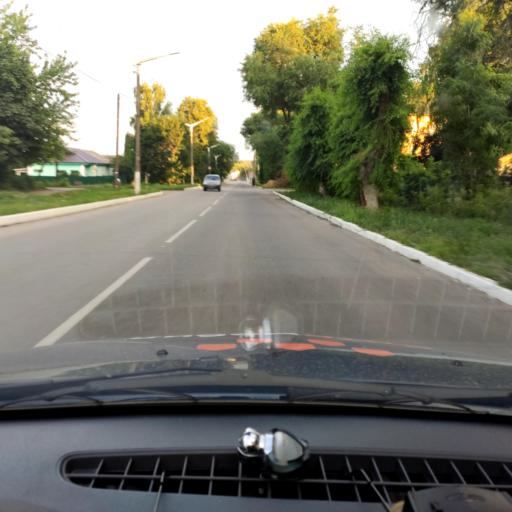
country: RU
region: Voronezj
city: Semiluki
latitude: 51.6853
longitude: 39.0403
